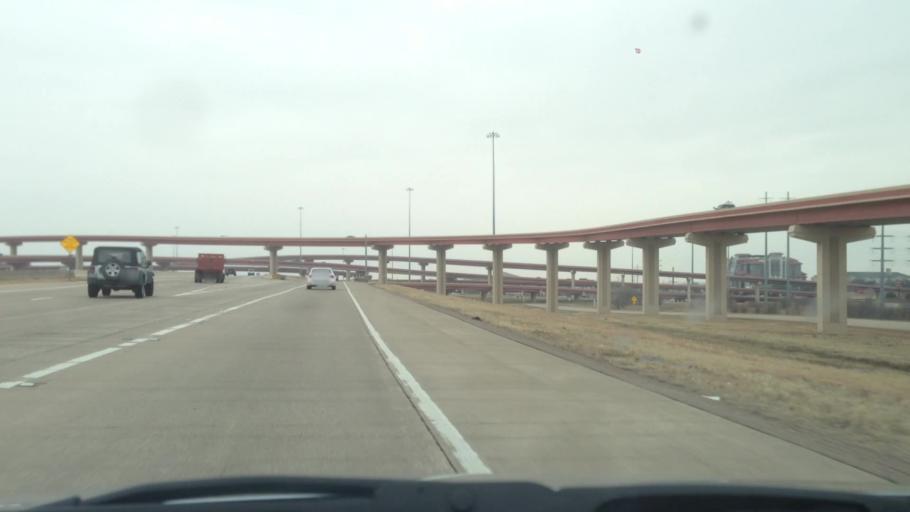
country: US
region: Texas
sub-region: Tarrant County
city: Euless
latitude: 32.8420
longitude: -97.0170
